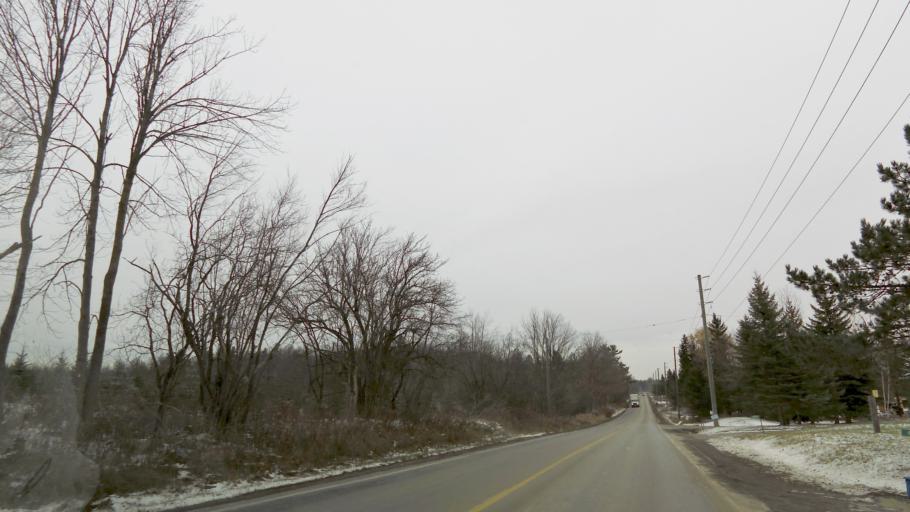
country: CA
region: Ontario
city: Vaughan
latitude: 43.8730
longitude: -79.6087
